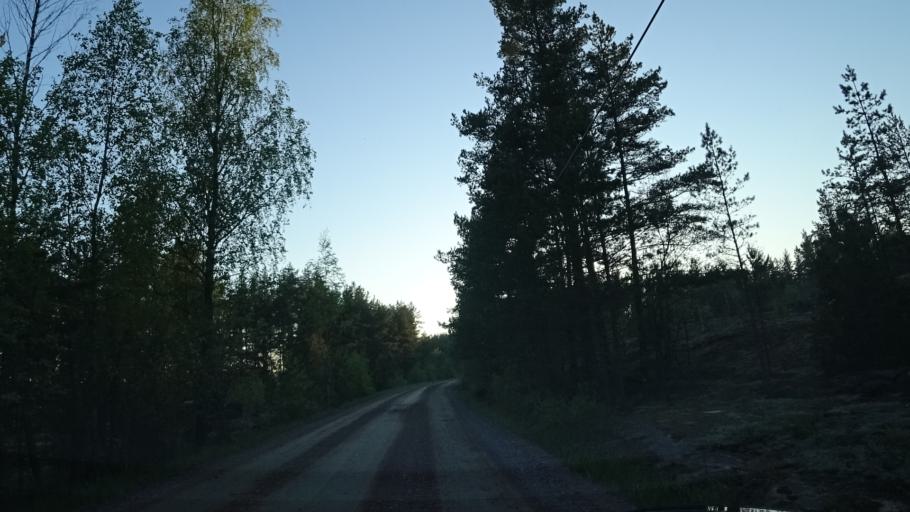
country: FI
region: Uusimaa
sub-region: Helsinki
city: Siuntio
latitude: 60.0635
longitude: 24.2256
